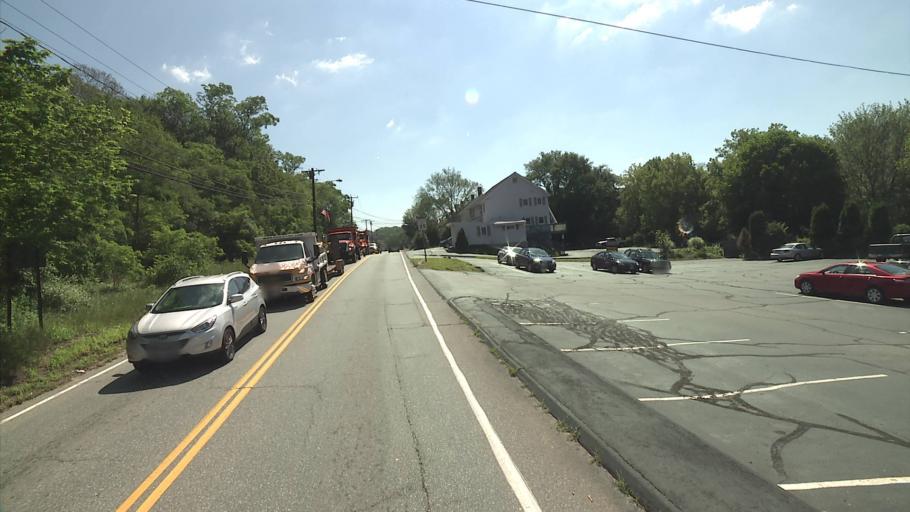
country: US
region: Connecticut
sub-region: Windham County
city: Moosup
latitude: 41.7195
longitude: -71.9030
